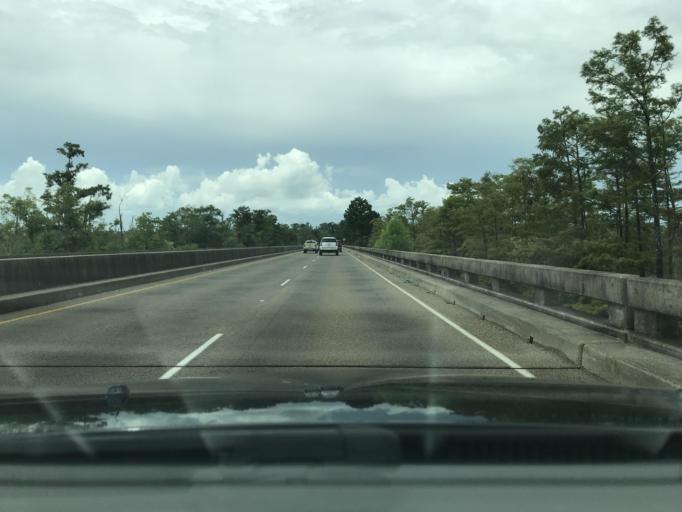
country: US
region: Louisiana
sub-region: Calcasieu Parish
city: Moss Bluff
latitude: 30.2920
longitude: -93.1924
